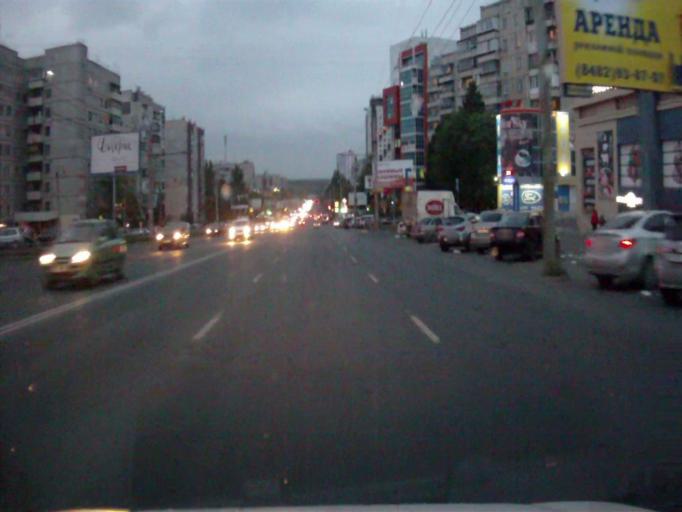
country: RU
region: Chelyabinsk
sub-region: Gorod Chelyabinsk
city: Chelyabinsk
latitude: 55.1856
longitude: 61.3325
